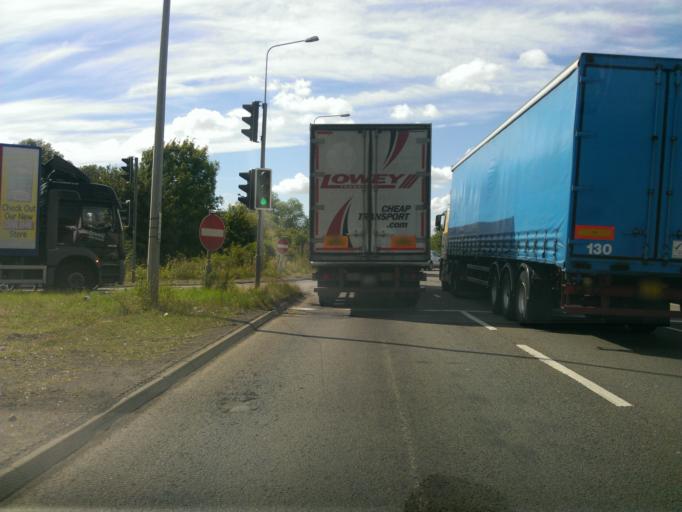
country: GB
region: England
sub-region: Cambridgeshire
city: Brampton
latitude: 52.3322
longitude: -0.2486
